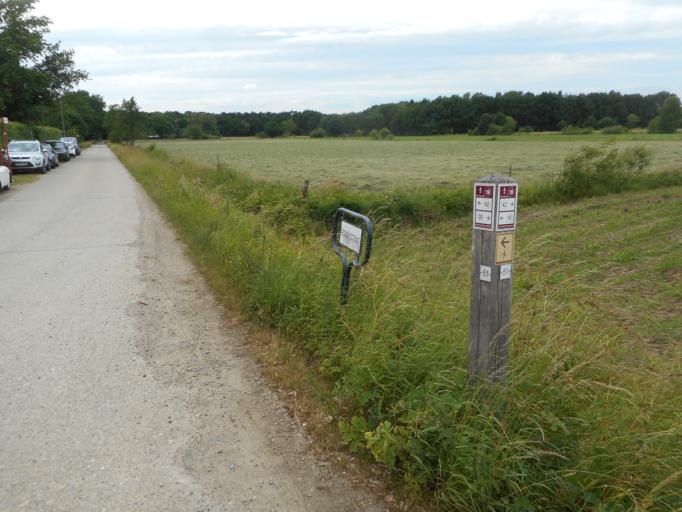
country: BE
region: Flanders
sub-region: Provincie Antwerpen
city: Zandhoven
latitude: 51.2428
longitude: 4.6702
